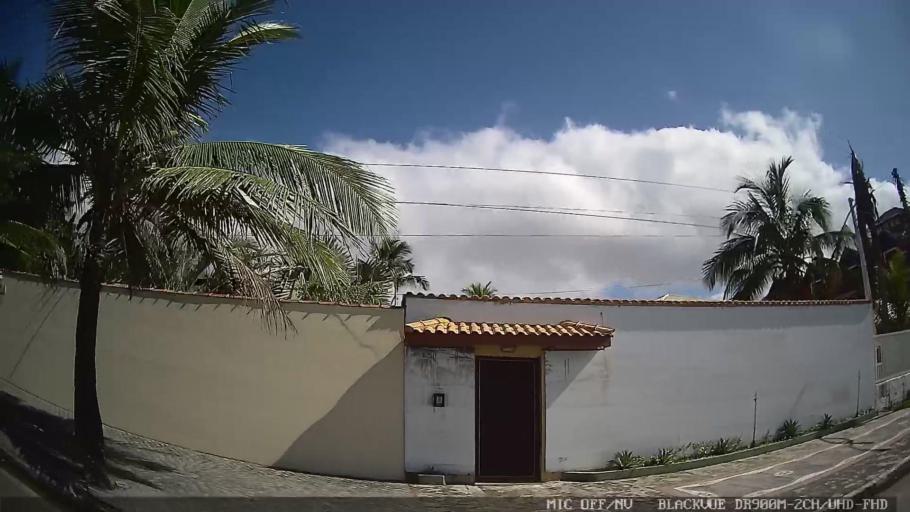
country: BR
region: Sao Paulo
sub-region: Peruibe
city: Peruibe
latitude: -24.3063
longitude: -46.9752
